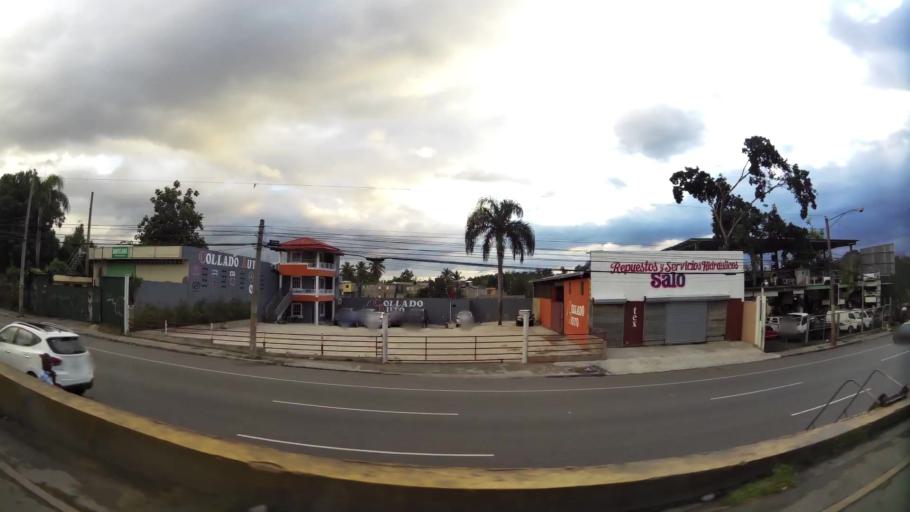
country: DO
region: Santo Domingo
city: Santo Domingo Oeste
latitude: 18.5367
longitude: -70.0174
